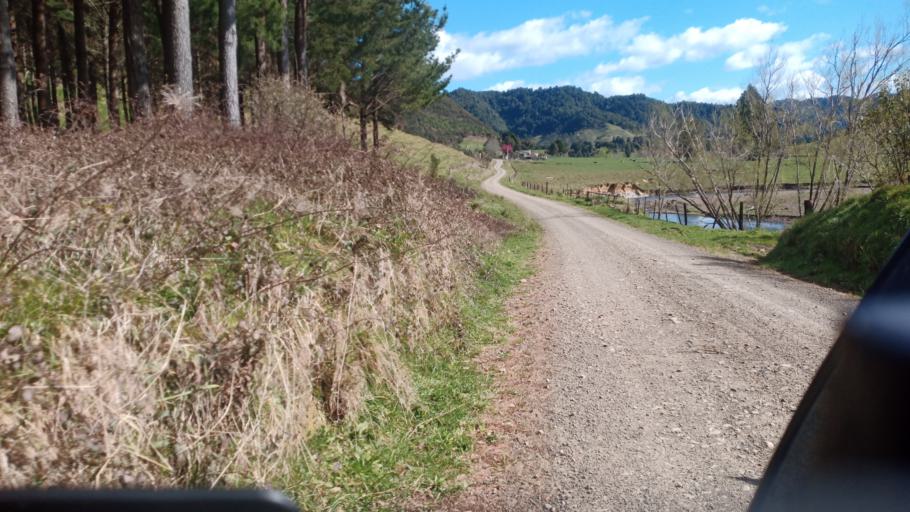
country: NZ
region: Bay of Plenty
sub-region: Opotiki District
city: Opotiki
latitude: -38.1102
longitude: 177.5226
